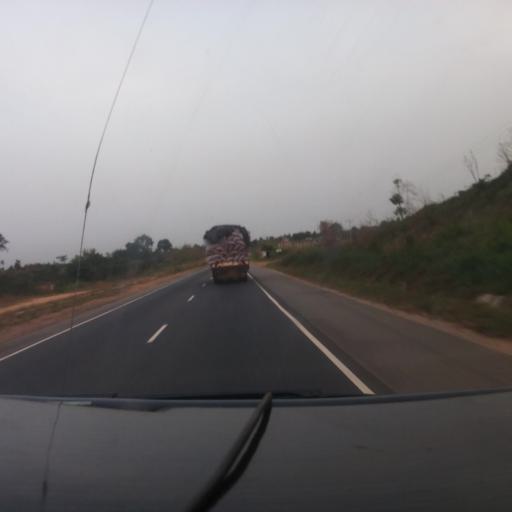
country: GH
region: Eastern
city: Nsawam
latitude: 5.8868
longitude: -0.3787
